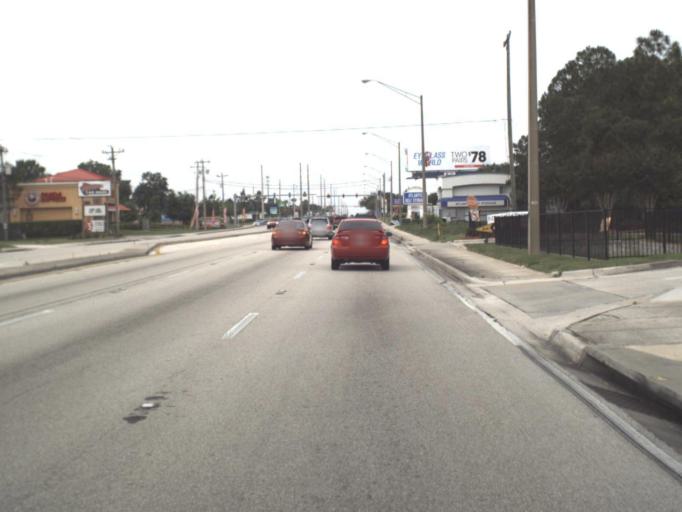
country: US
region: Florida
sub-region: Clay County
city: Lakeside
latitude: 30.1409
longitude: -81.7692
